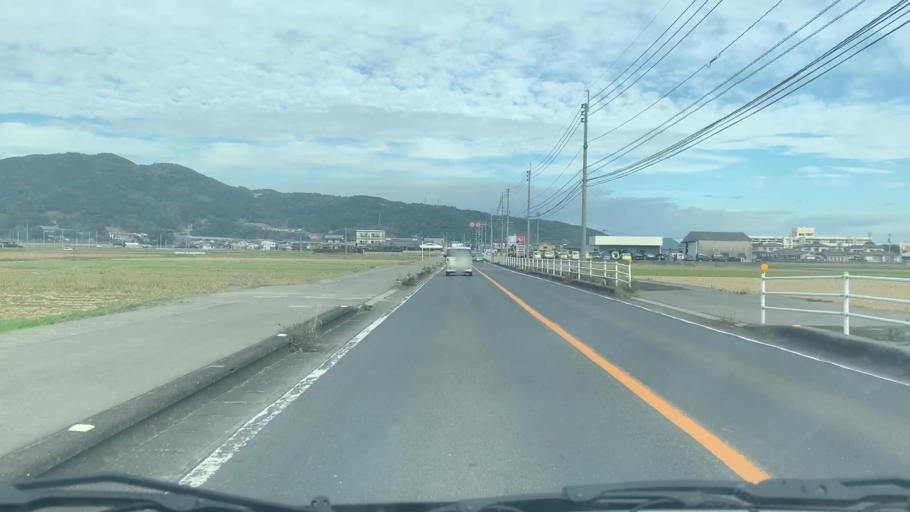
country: JP
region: Saga Prefecture
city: Karatsu
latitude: 33.4012
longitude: 129.9871
